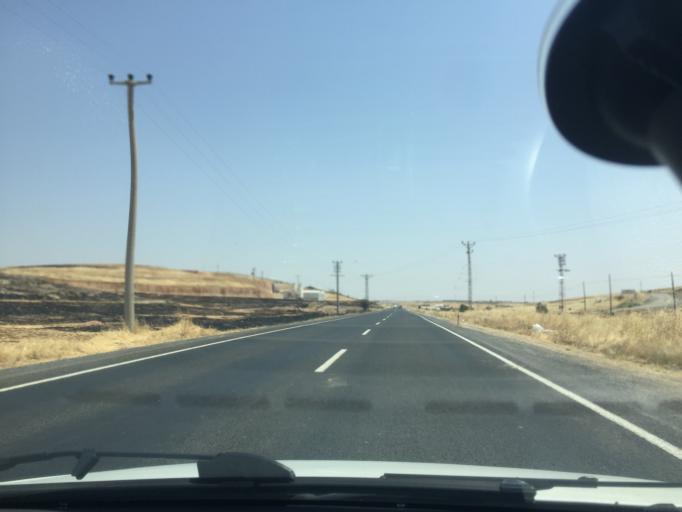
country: TR
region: Mardin
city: Kindirip
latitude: 37.4601
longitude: 41.2363
